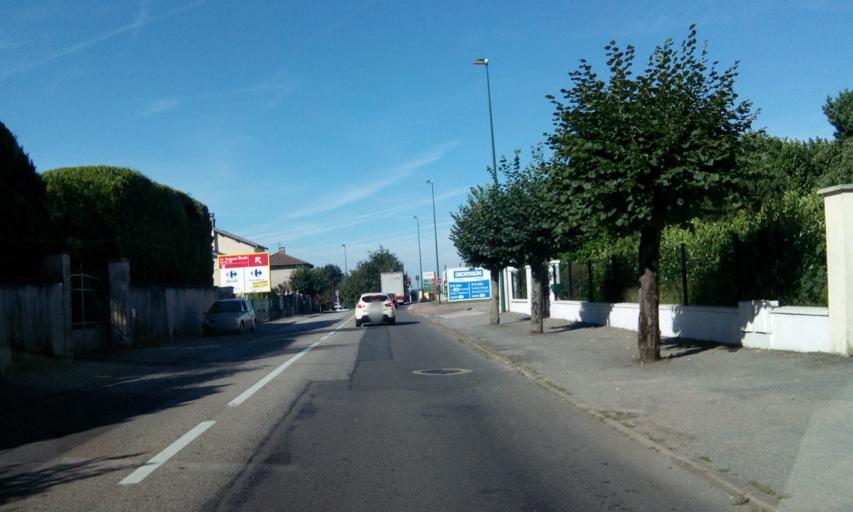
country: FR
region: Limousin
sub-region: Departement de la Haute-Vienne
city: Panazol
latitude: 45.8281
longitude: 1.2935
